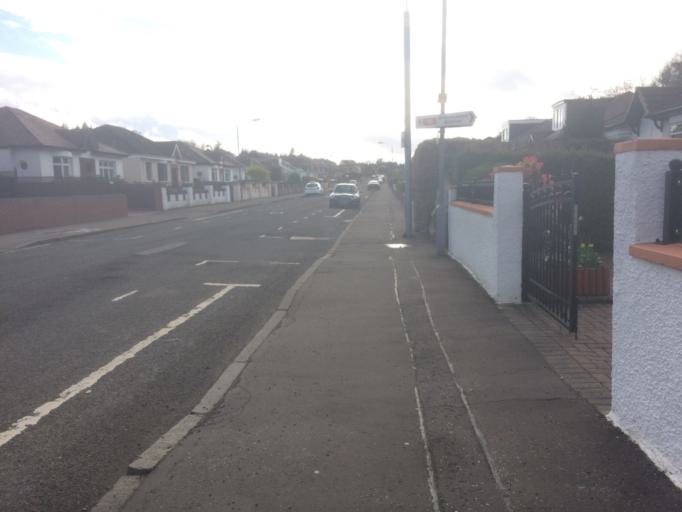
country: GB
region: Scotland
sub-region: East Renfrewshire
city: Giffnock
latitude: 55.7934
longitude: -4.2897
